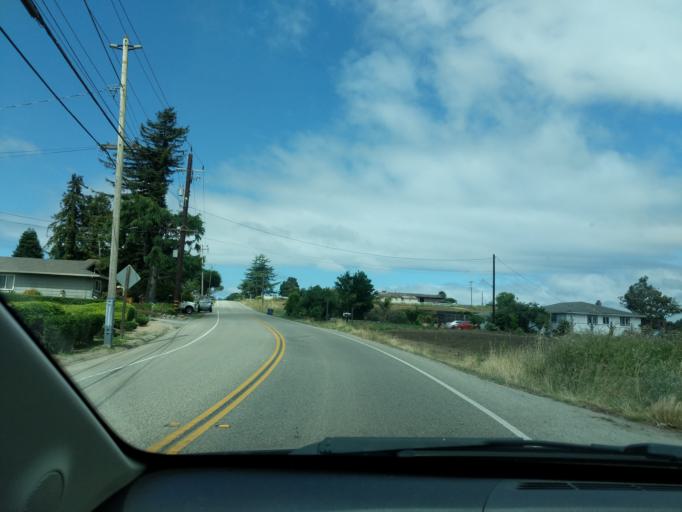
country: US
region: California
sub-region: Santa Cruz County
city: Freedom
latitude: 36.9404
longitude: -121.7966
